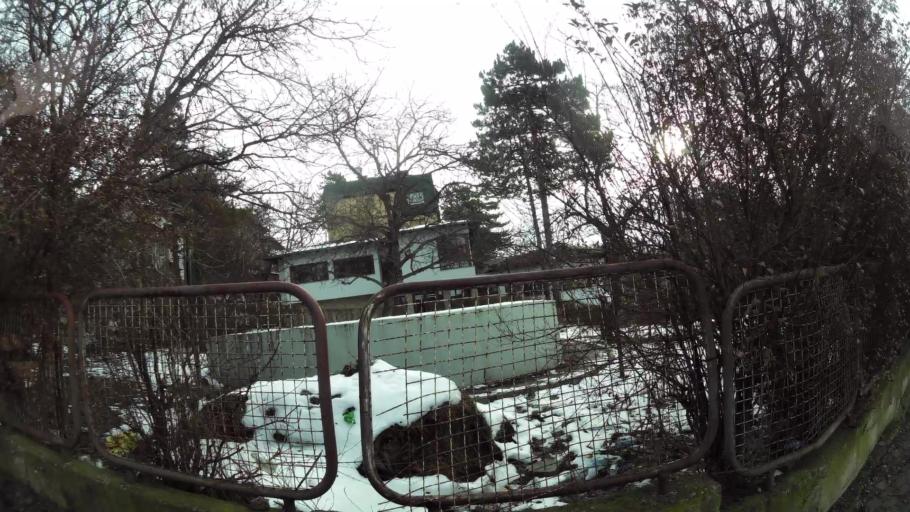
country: XK
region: Pristina
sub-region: Komuna e Prishtines
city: Pristina
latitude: 42.6665
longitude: 21.1777
